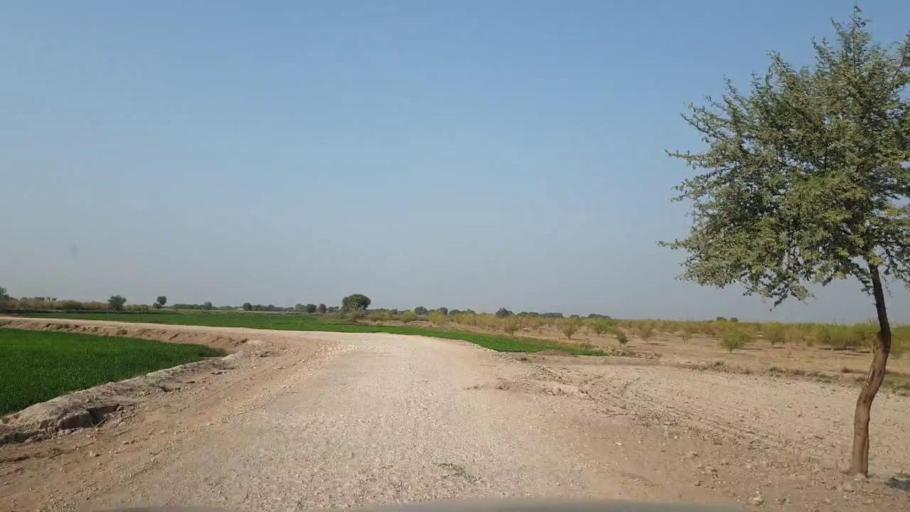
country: PK
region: Sindh
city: Tando Allahyar
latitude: 25.5763
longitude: 68.7951
